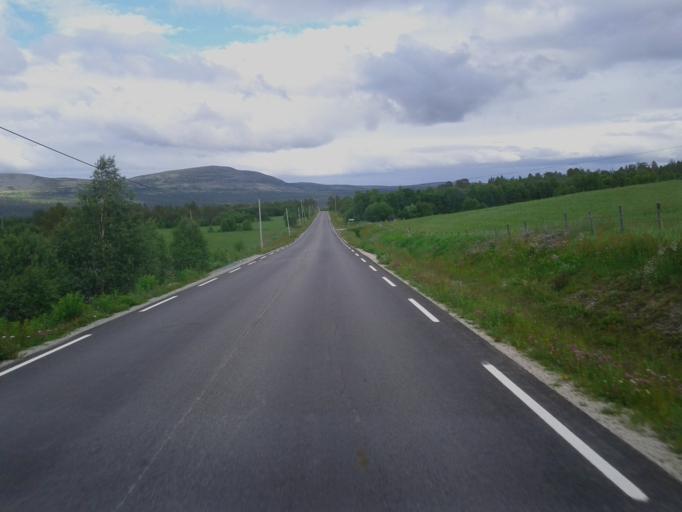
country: NO
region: Sor-Trondelag
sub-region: Roros
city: Roros
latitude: 62.3068
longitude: 11.6942
